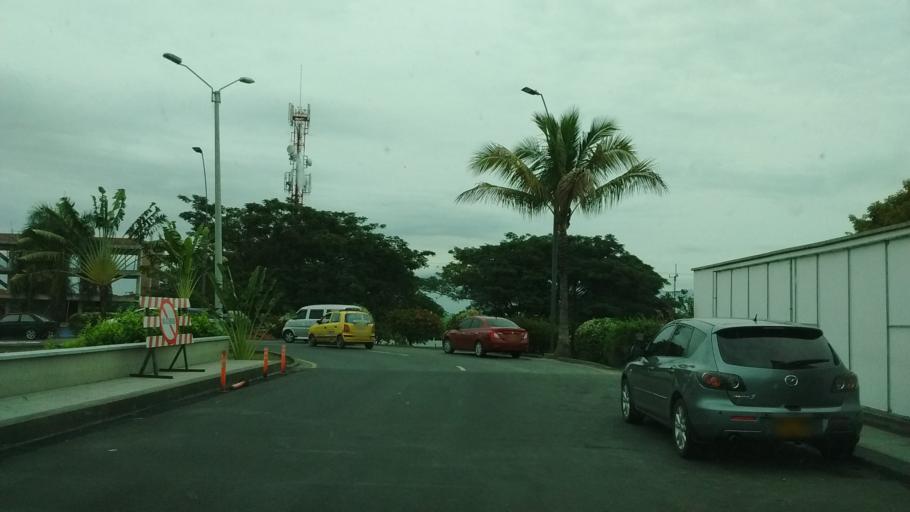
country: CO
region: Valle del Cauca
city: Palmira
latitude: 3.5367
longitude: -76.3885
